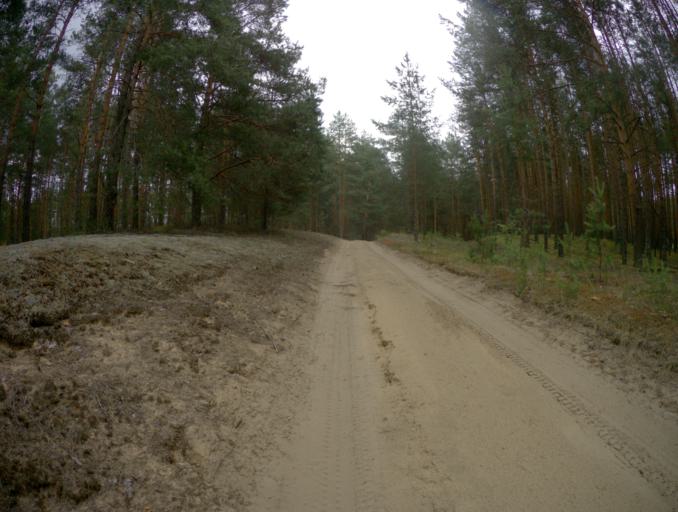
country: RU
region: Nizjnij Novgorod
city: Frolishchi
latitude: 56.3225
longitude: 42.7136
